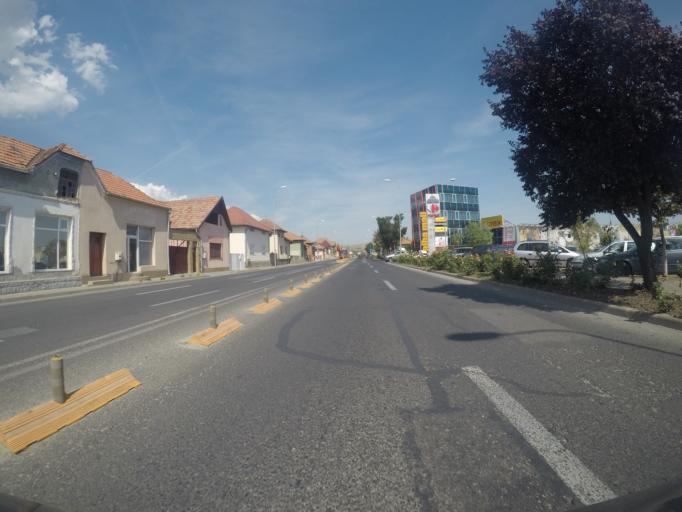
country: RO
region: Alba
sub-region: Municipiul Alba Iulia
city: Alba Iulia
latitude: 46.0801
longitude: 23.5837
